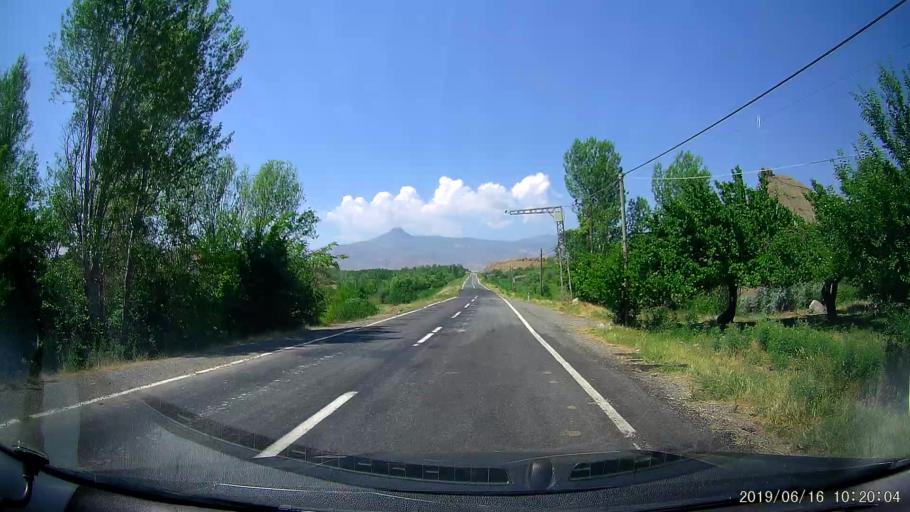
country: TR
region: Igdir
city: Tuzluca
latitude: 40.1508
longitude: 43.6511
